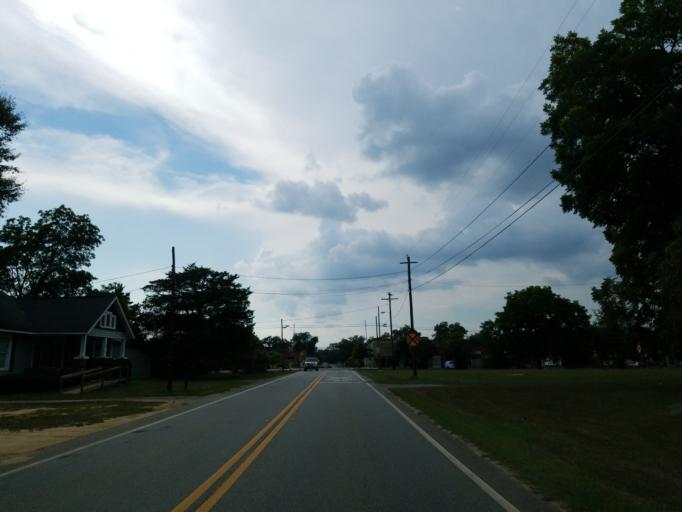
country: US
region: Georgia
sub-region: Dooly County
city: Unadilla
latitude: 32.2610
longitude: -83.7342
